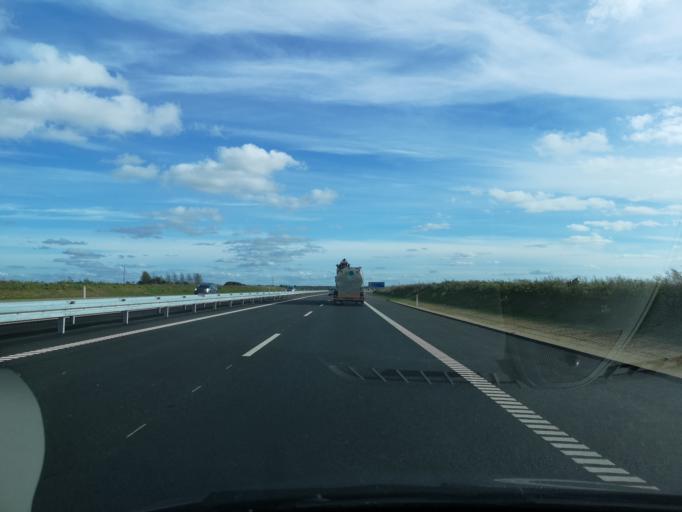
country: DK
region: Central Jutland
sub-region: Holstebro Kommune
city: Holstebro
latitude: 56.3732
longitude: 8.7089
